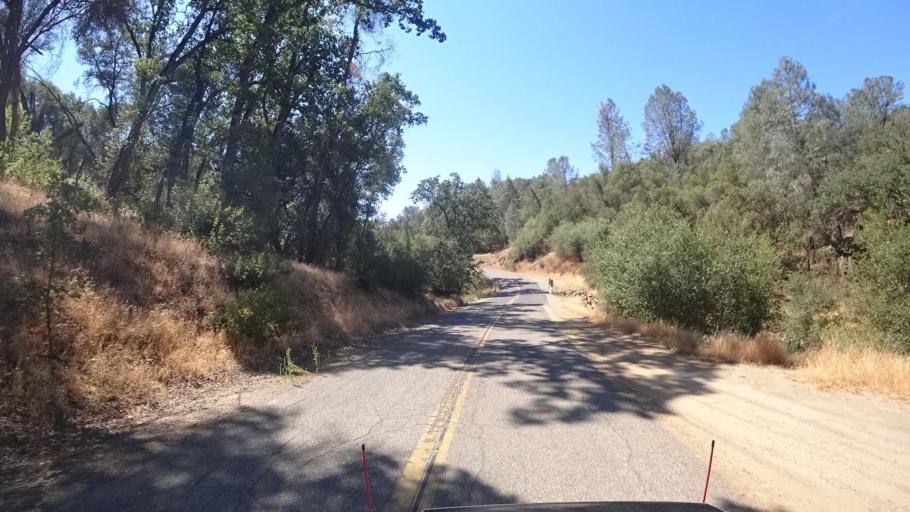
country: US
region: California
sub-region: Mariposa County
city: Mariposa
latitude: 37.4104
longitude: -119.9654
